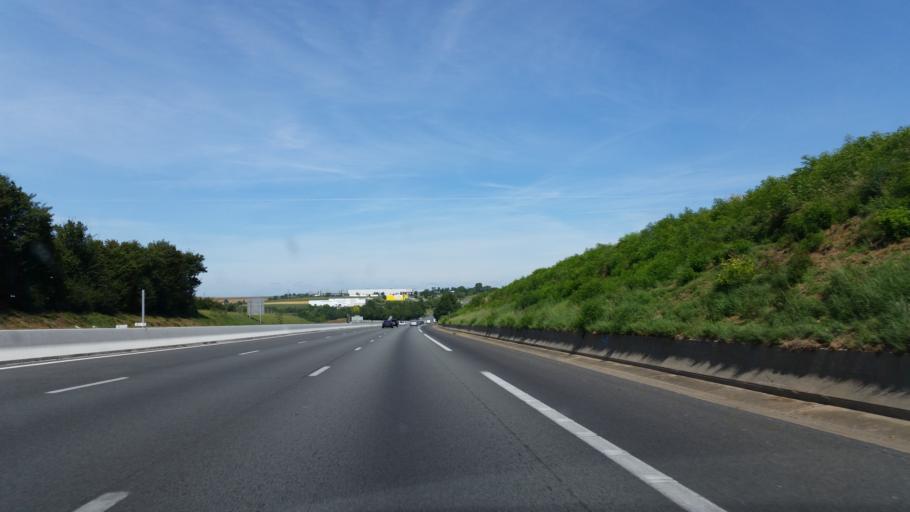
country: FR
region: Nord-Pas-de-Calais
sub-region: Departement du Pas-de-Calais
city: Feuchy
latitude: 50.2452
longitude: 2.8556
